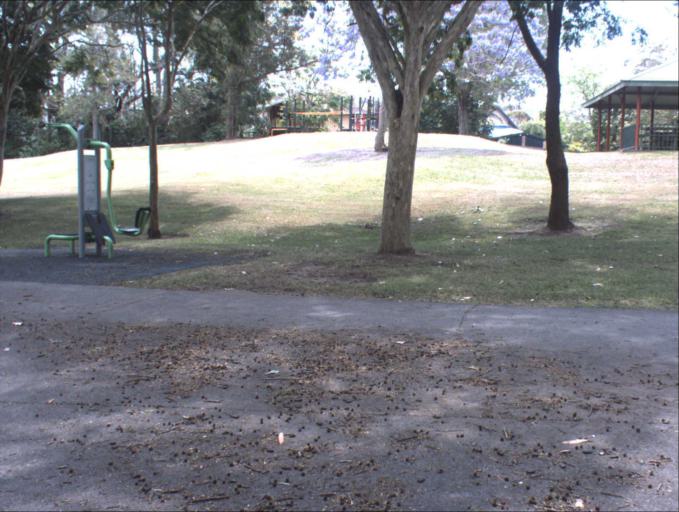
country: AU
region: Queensland
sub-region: Logan
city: Slacks Creek
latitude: -27.6447
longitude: 153.1711
